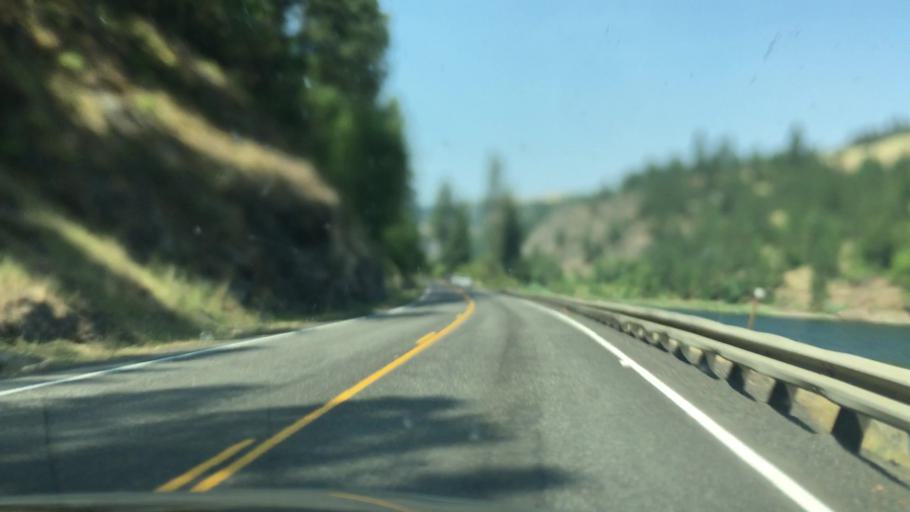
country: US
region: Idaho
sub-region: Clearwater County
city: Orofino
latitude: 46.4970
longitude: -116.4136
